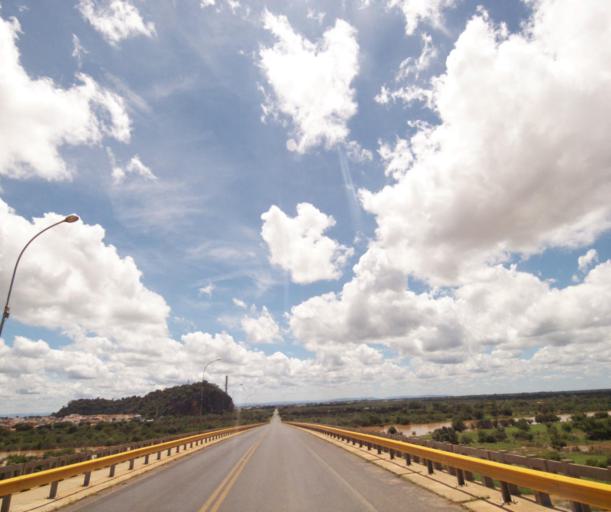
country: BR
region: Bahia
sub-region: Bom Jesus Da Lapa
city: Bom Jesus da Lapa
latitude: -13.2584
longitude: -43.4318
